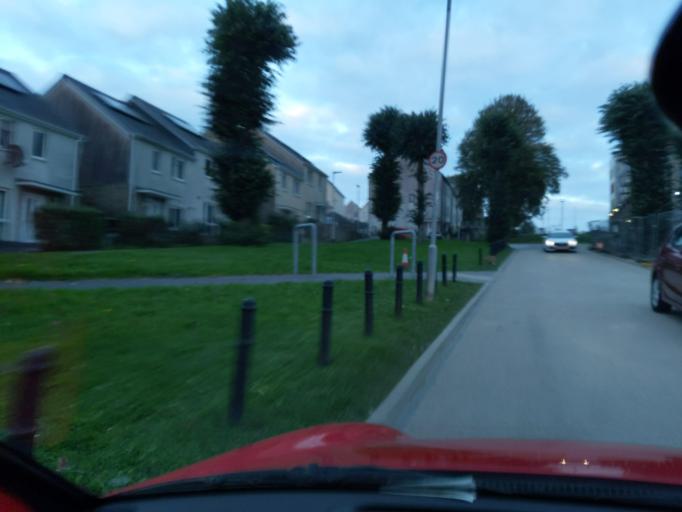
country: GB
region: England
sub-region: Cornwall
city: Millbrook
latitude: 50.3928
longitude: -4.1683
